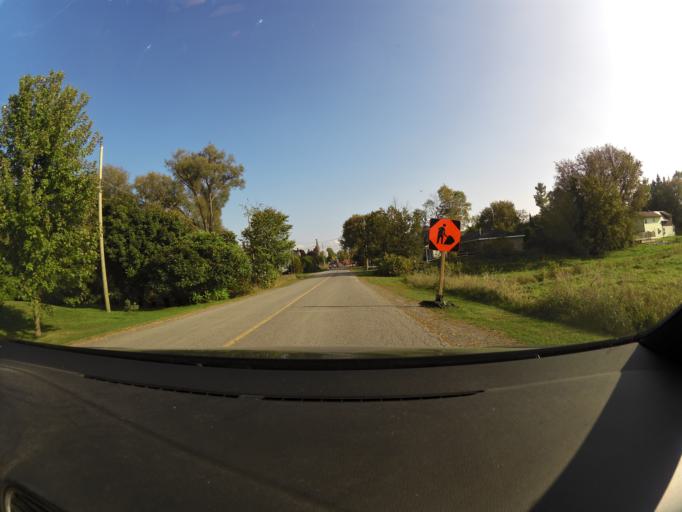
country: CA
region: Ontario
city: Arnprior
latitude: 45.3931
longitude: -76.1904
